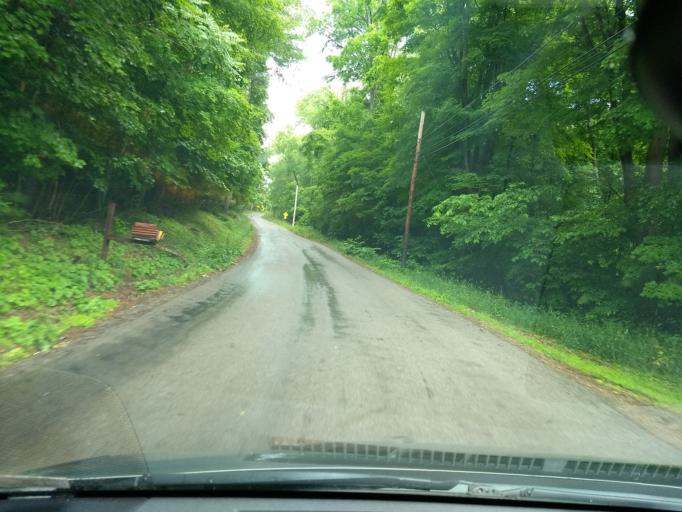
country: US
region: Pennsylvania
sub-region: Westmoreland County
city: Avonmore
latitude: 40.5326
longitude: -79.4912
